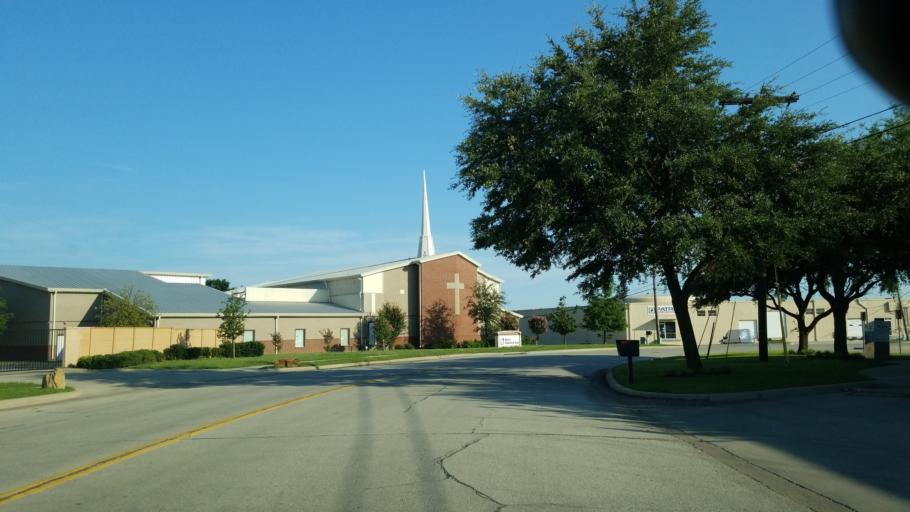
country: US
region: Texas
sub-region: Dallas County
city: Farmers Branch
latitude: 32.9351
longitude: -96.8991
